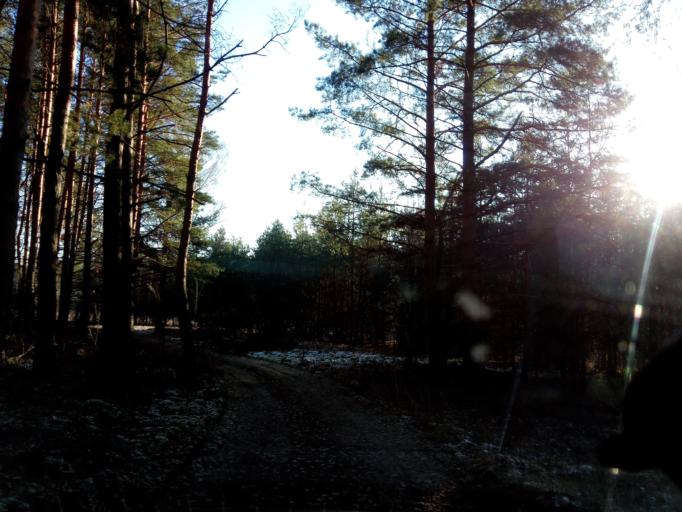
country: LT
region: Alytaus apskritis
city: Druskininkai
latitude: 53.9498
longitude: 23.8735
